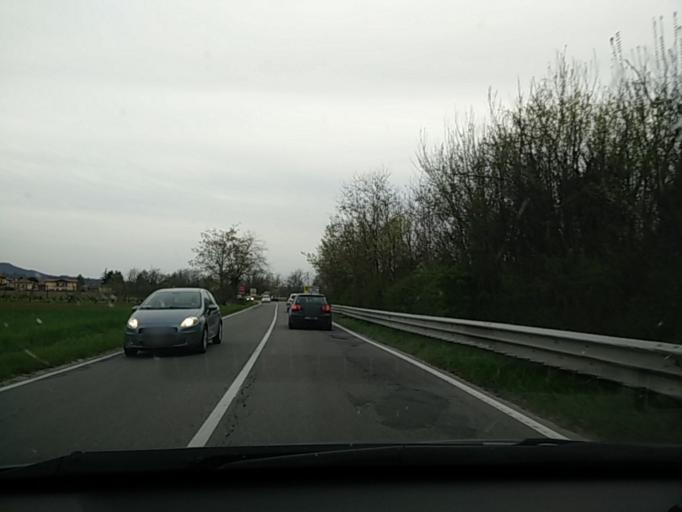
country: IT
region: Lombardy
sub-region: Provincia di Pavia
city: Rivanazzano
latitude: 44.9385
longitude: 9.0236
